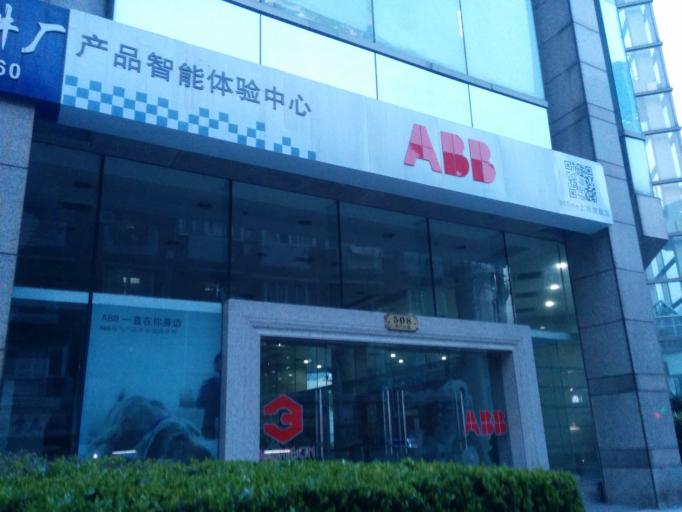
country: CN
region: Shanghai Shi
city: Hongkou
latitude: 31.2400
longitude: 121.4723
